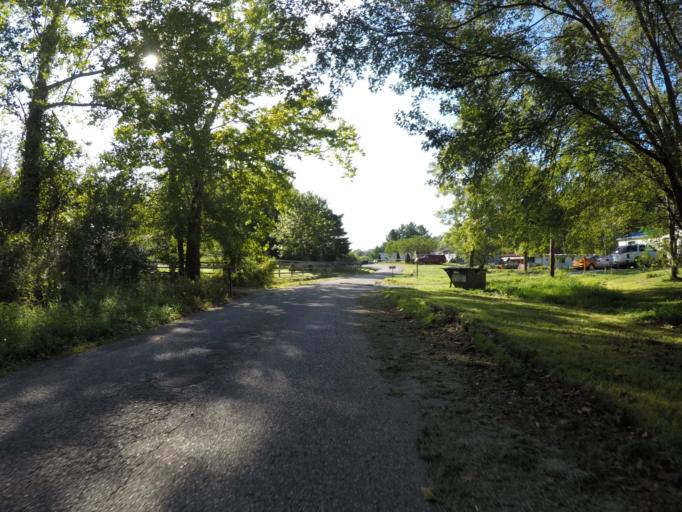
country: US
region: Ohio
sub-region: Lawrence County
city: Burlington
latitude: 38.5030
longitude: -82.5158
